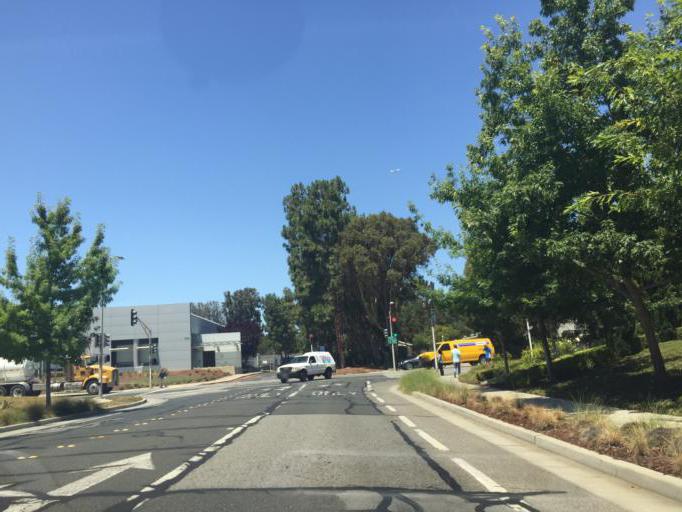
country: US
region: California
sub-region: Santa Clara County
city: Stanford
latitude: 37.4088
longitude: -122.1467
